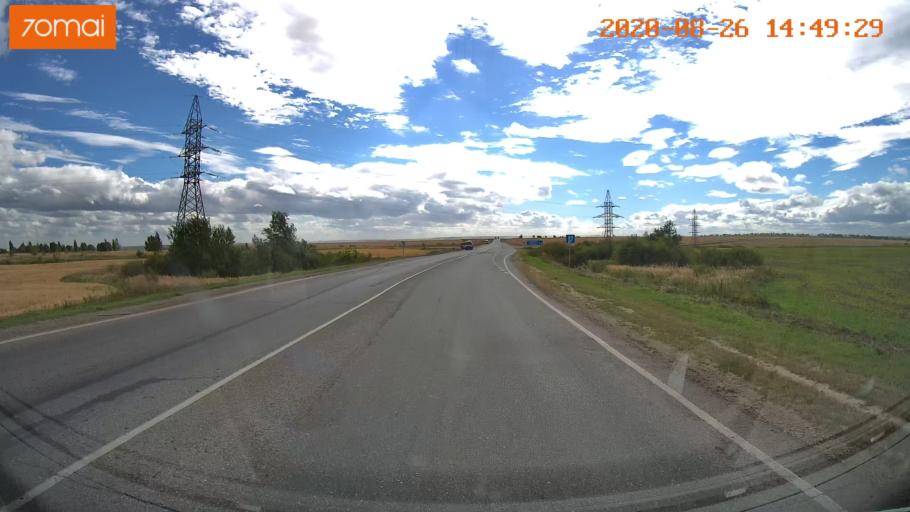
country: RU
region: Rjazan
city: Mikhaylov
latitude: 54.2565
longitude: 38.9997
